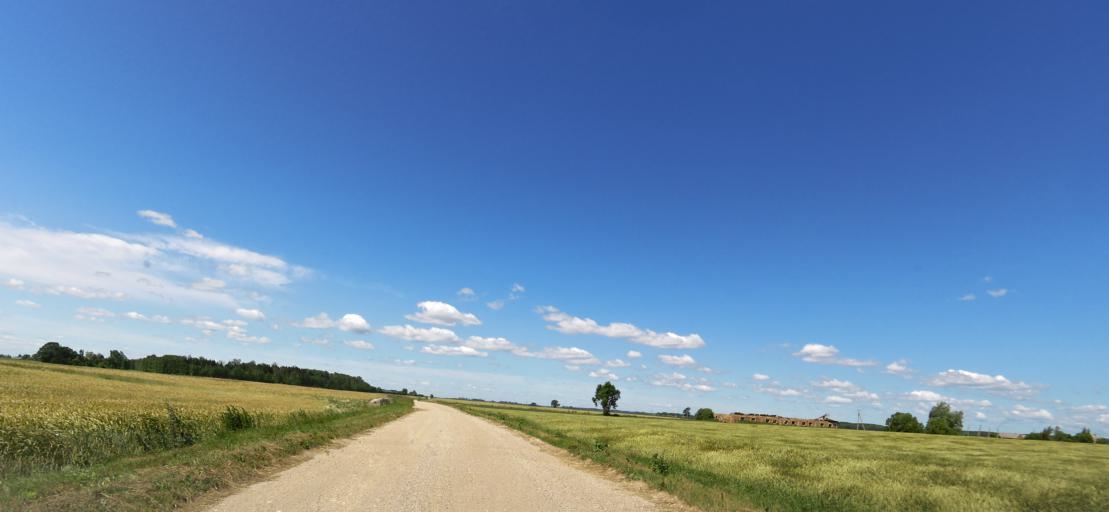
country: LT
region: Panevezys
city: Pasvalys
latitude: 56.2619
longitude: 24.5181
